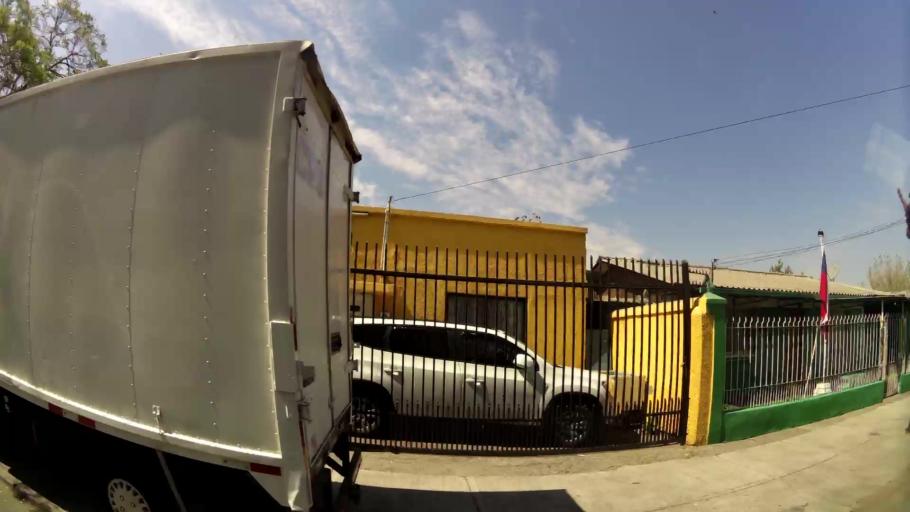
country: CL
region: Santiago Metropolitan
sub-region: Provincia de Santiago
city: La Pintana
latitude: -33.5507
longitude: -70.6650
